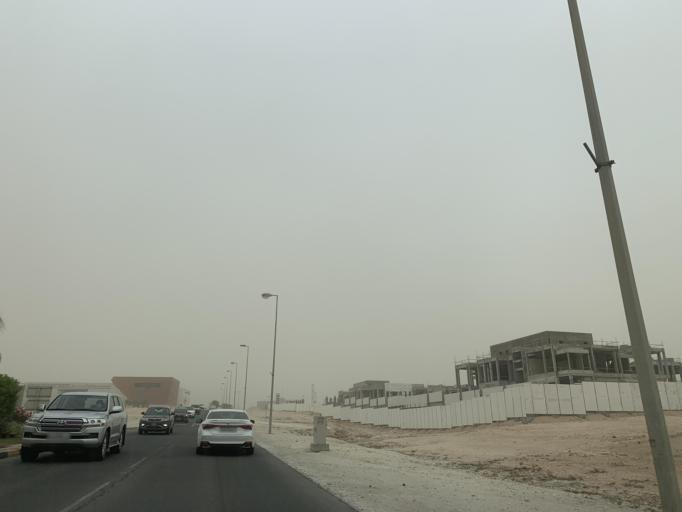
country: BH
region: Central Governorate
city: Madinat Hamad
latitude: 26.1361
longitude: 50.5161
